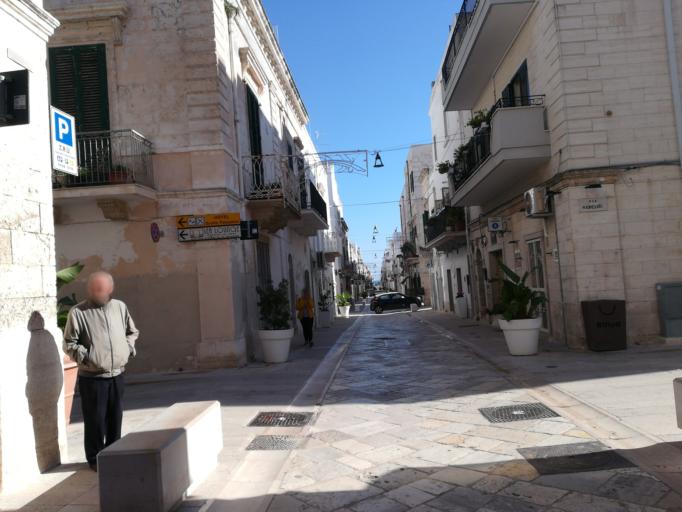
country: IT
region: Apulia
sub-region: Provincia di Bari
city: Polignano a Mare
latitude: 40.9954
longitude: 17.2212
